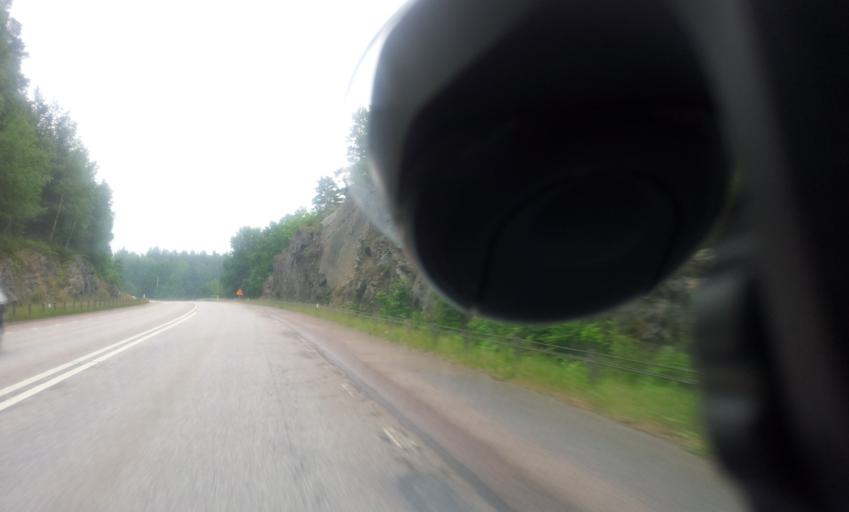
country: SE
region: Kalmar
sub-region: Vasterviks Kommun
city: Ankarsrum
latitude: 57.6690
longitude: 16.4416
